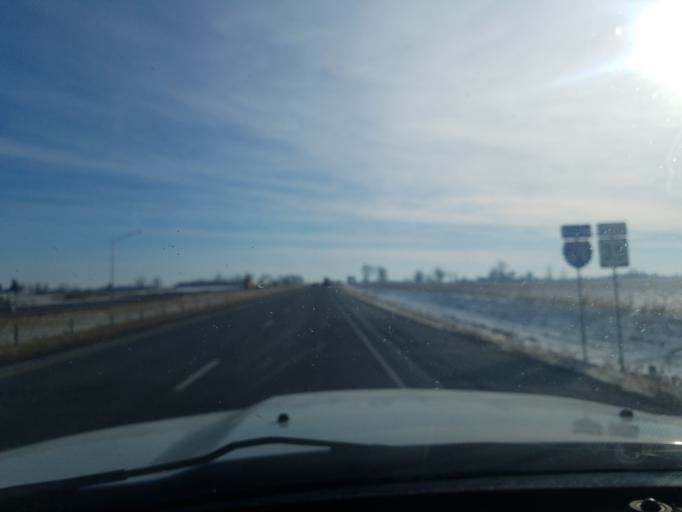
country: US
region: Indiana
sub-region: Grant County
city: Fairmount
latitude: 40.3480
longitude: -85.5589
